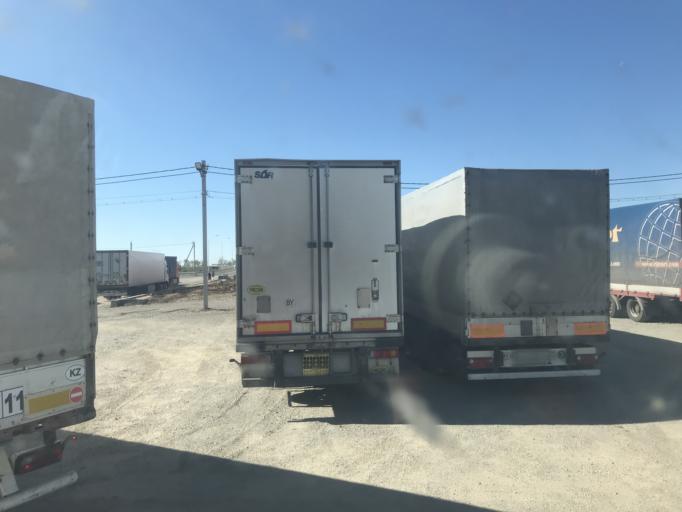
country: KZ
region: Aqtoebe
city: Aqtobe
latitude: 50.2966
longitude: 57.4761
